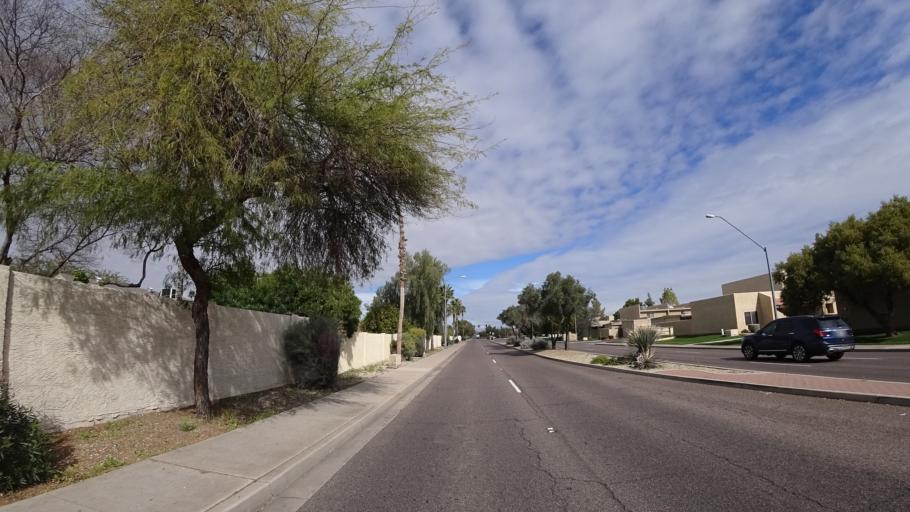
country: US
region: Arizona
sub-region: Maricopa County
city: Peoria
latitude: 33.6160
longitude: -112.1859
